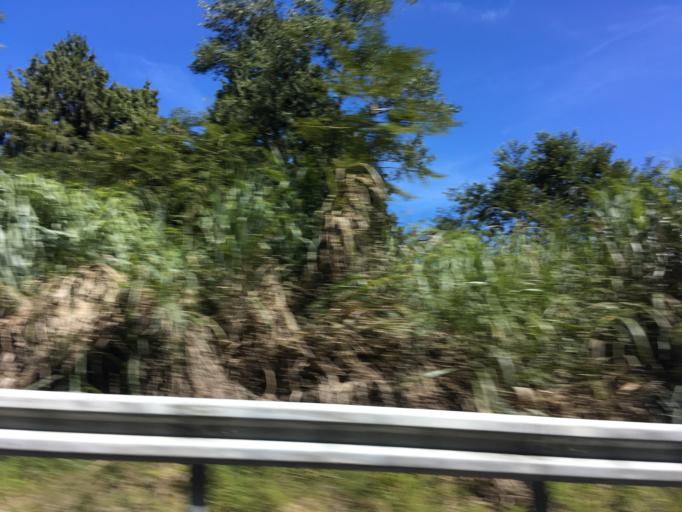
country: TW
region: Taiwan
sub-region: Yilan
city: Yilan
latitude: 24.5239
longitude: 121.5170
